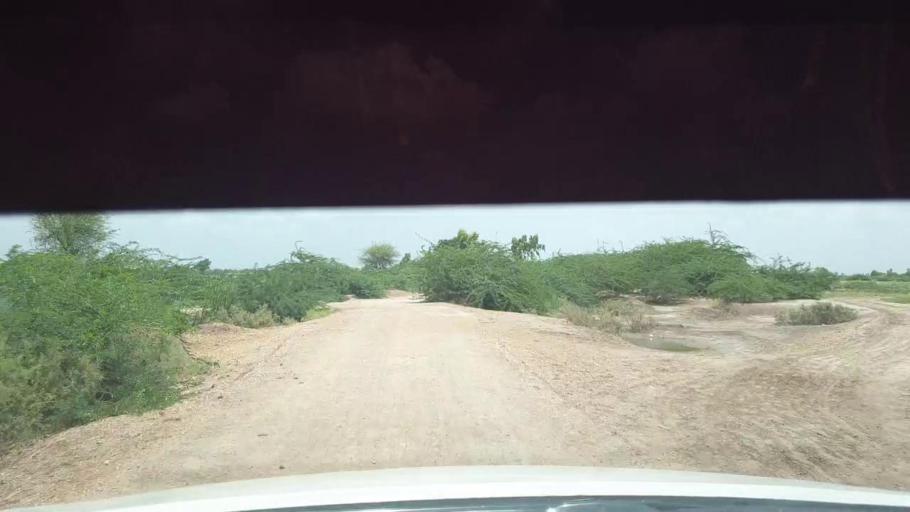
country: PK
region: Sindh
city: Kadhan
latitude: 24.4863
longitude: 69.0030
